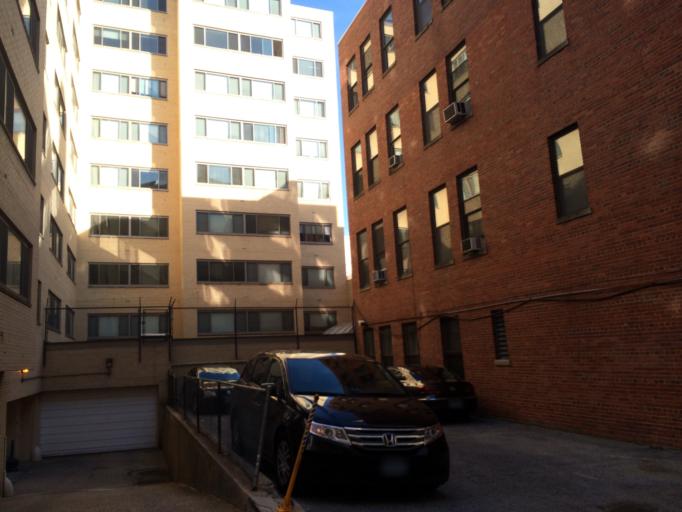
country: US
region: Washington, D.C.
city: Washington, D.C.
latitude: 38.8964
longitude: -77.0473
